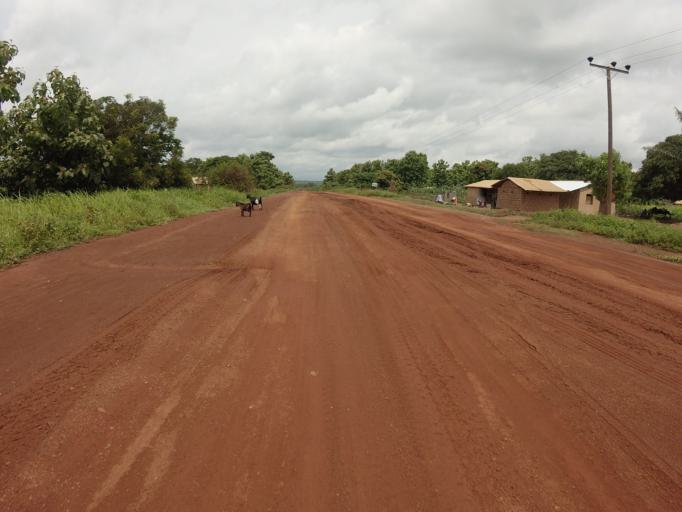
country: GH
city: Kpandae
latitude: 8.4115
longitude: 0.3936
